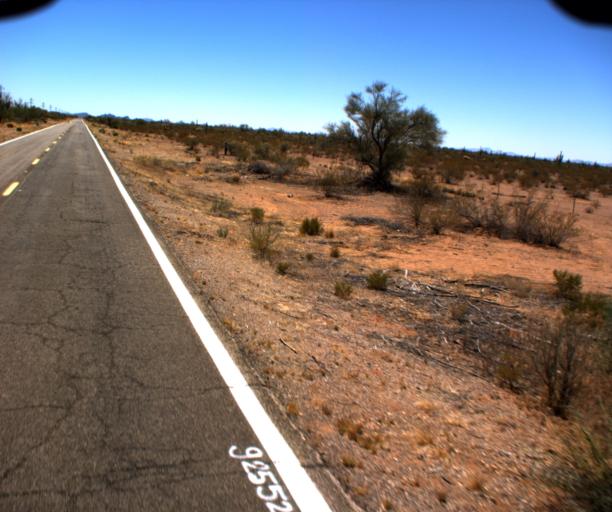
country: US
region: Arizona
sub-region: Pima County
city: Sells
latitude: 32.0860
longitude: -112.0542
